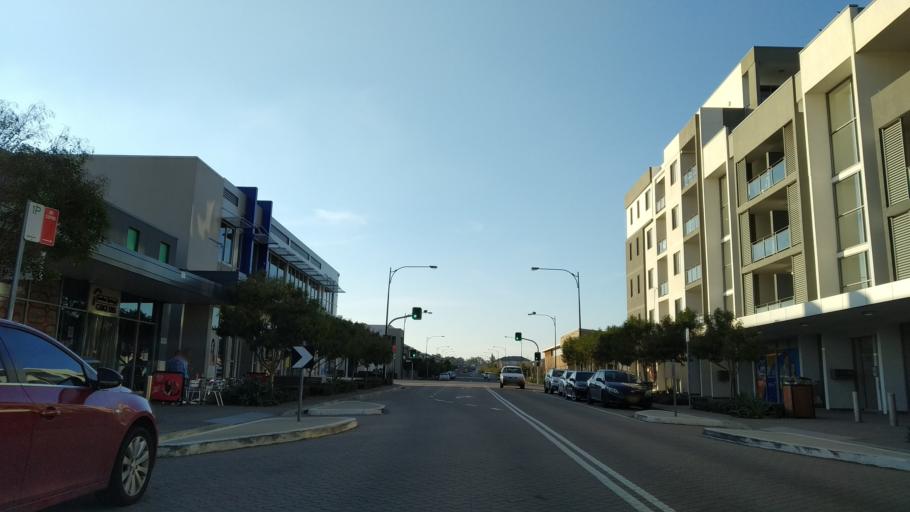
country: AU
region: New South Wales
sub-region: Penrith Municipality
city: Werrington Downs
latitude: -33.7269
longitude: 150.7258
